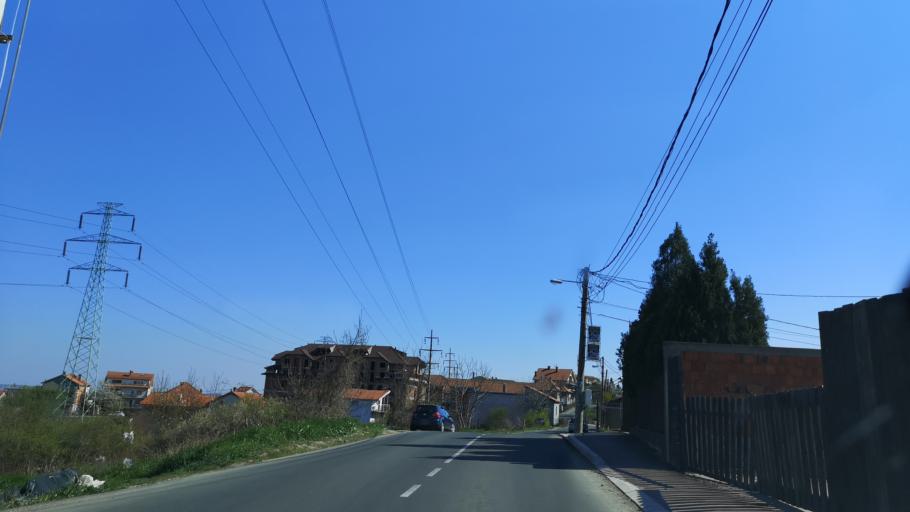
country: RS
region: Central Serbia
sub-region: Belgrade
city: Zvezdara
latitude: 44.7625
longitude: 20.5342
